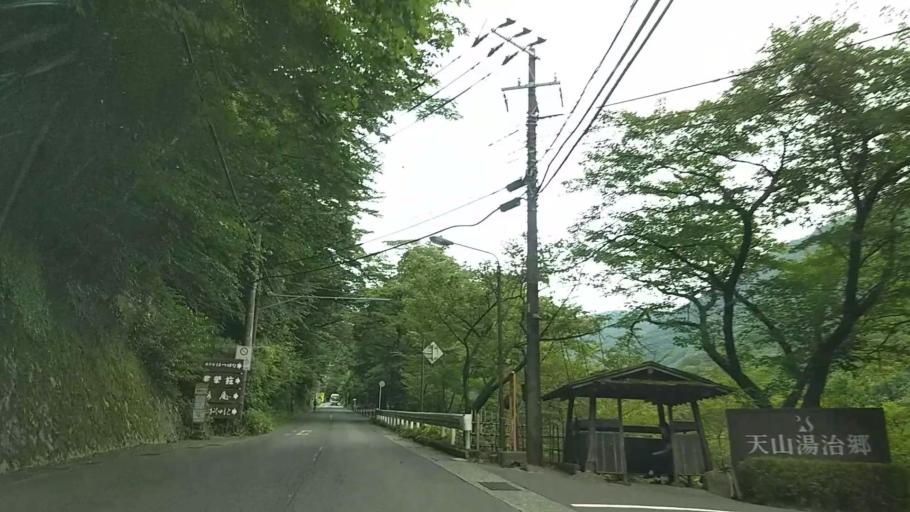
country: JP
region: Kanagawa
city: Hakone
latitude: 35.2250
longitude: 139.0904
